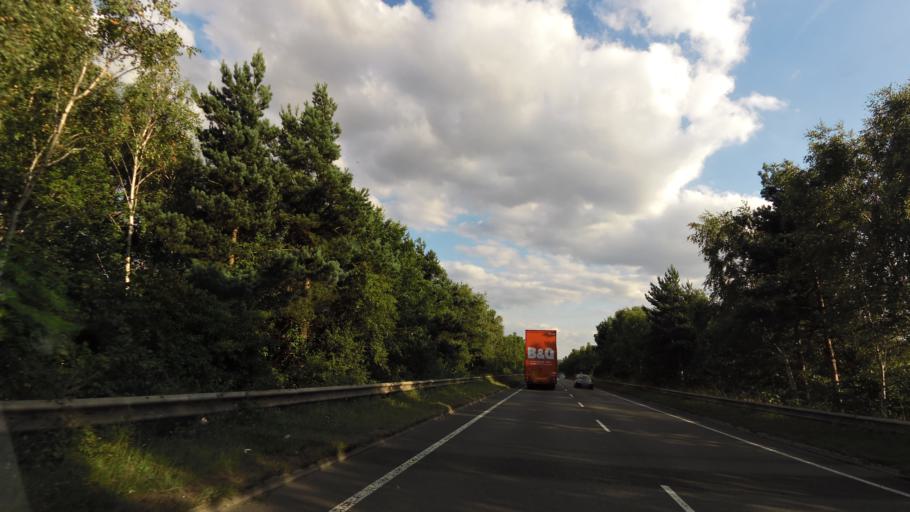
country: GB
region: England
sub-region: Nottinghamshire
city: Worksop
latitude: 53.3195
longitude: -1.1530
